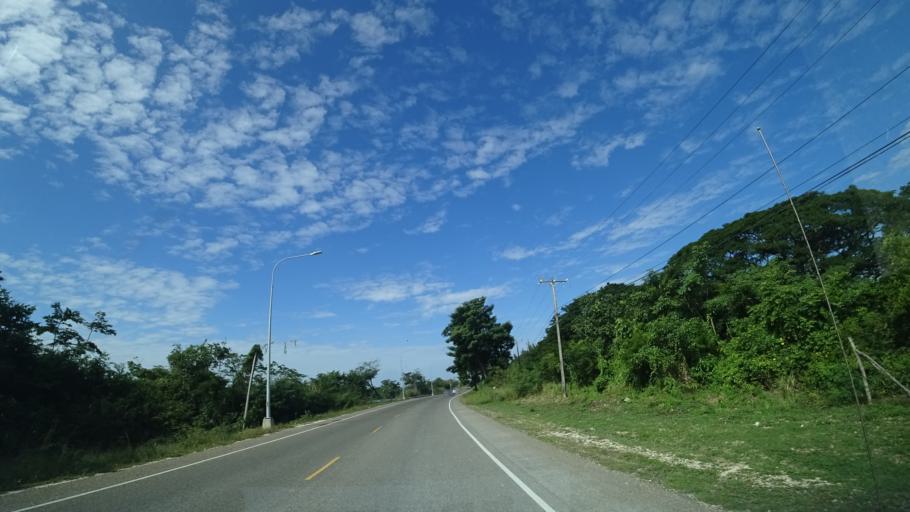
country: BZ
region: Belize
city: Belize City
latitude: 17.5450
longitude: -88.2720
